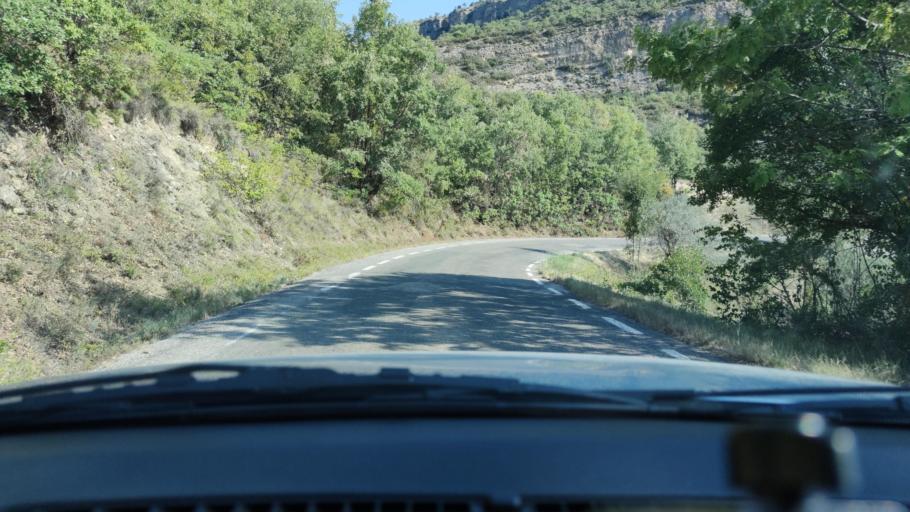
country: ES
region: Catalonia
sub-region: Provincia de Lleida
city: Llimiana
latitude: 42.0838
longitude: 0.8458
